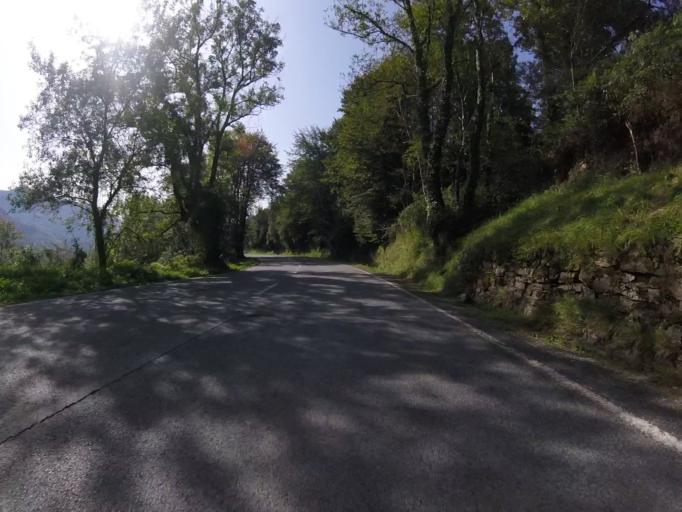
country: ES
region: Navarre
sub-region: Provincia de Navarra
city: Zugarramurdi
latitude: 43.2329
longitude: -1.4981
